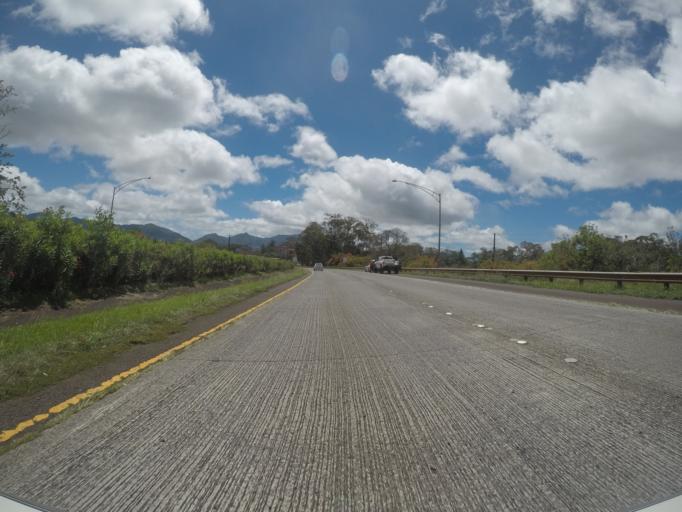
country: US
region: Hawaii
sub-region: Honolulu County
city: Wahiawa
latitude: 21.4902
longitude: -158.0292
